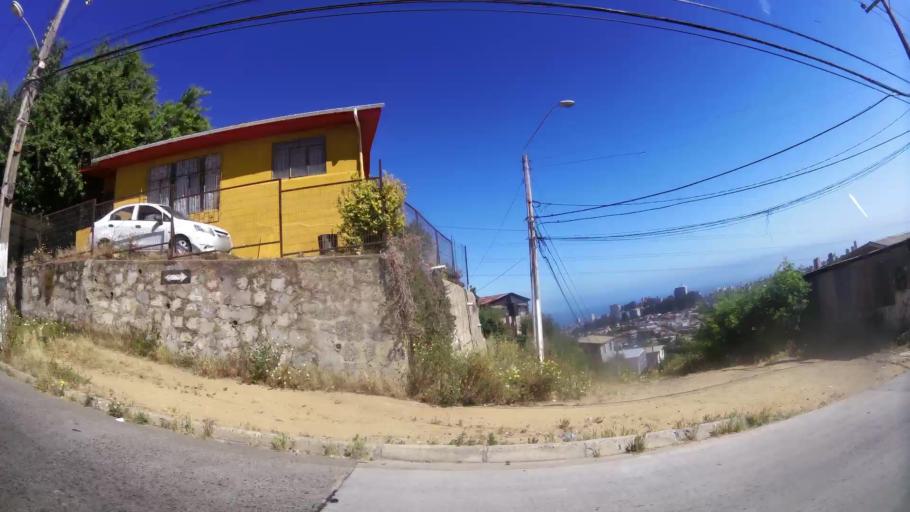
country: CL
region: Valparaiso
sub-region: Provincia de Valparaiso
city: Valparaiso
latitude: -33.0701
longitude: -71.5836
